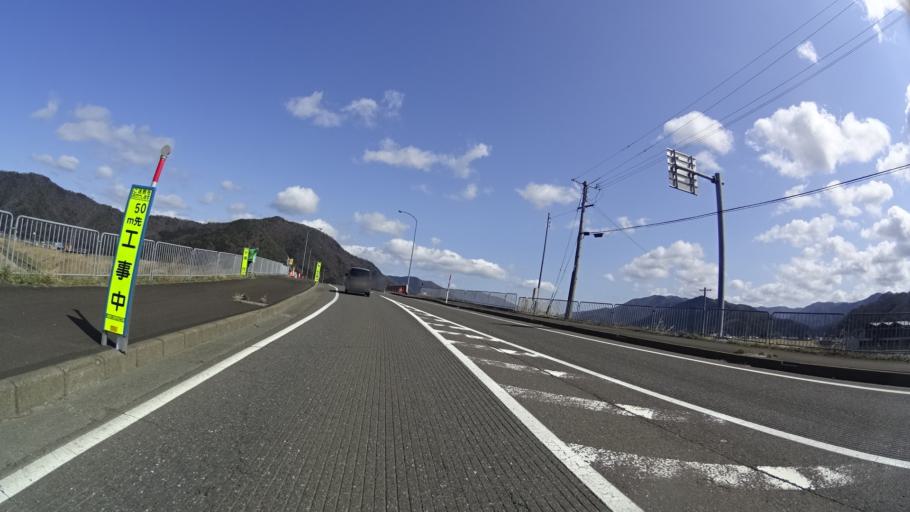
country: JP
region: Fukui
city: Obama
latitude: 35.4870
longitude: 135.7857
